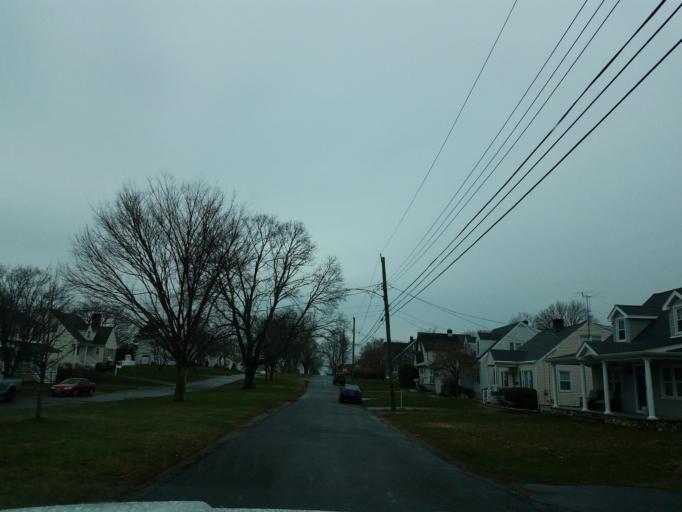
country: US
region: Connecticut
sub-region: Fairfield County
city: Stratford
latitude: 41.1541
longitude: -73.1281
